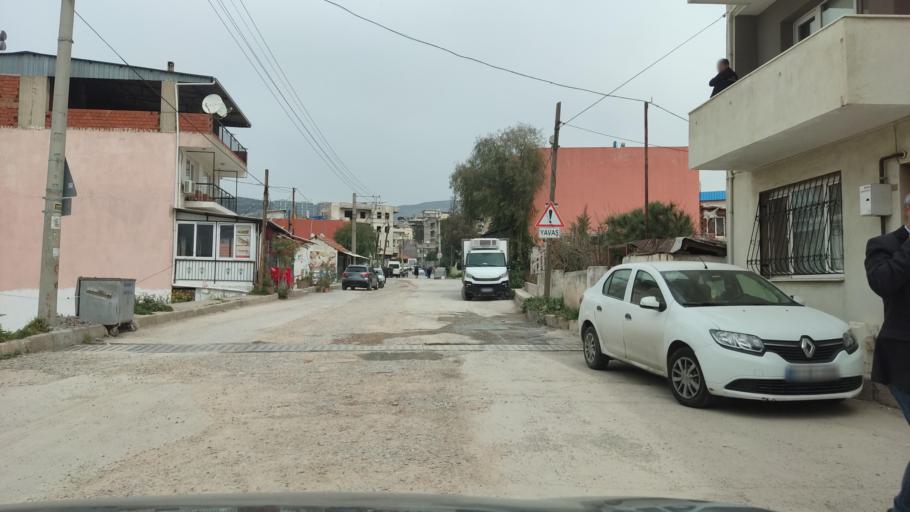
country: TR
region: Izmir
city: Karsiyaka
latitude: 38.4953
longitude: 27.0697
